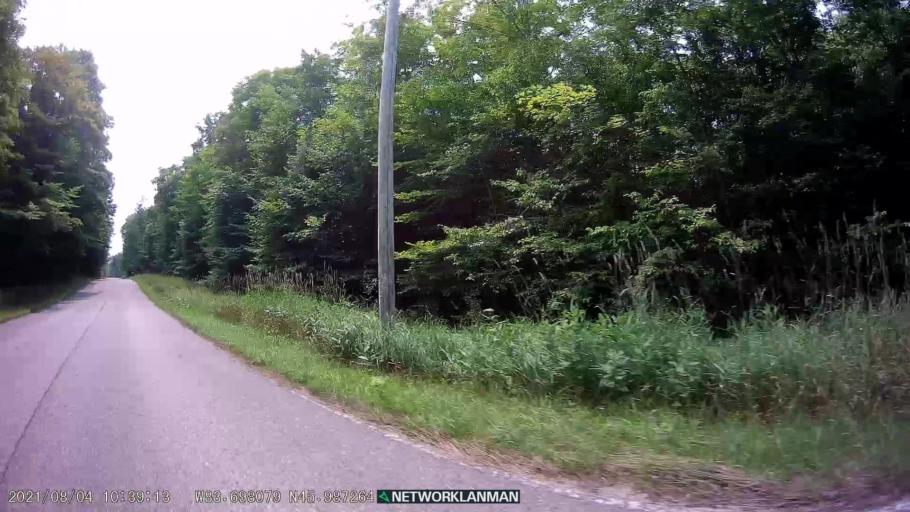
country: CA
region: Ontario
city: Thessalon
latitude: 45.9861
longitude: -83.6979
